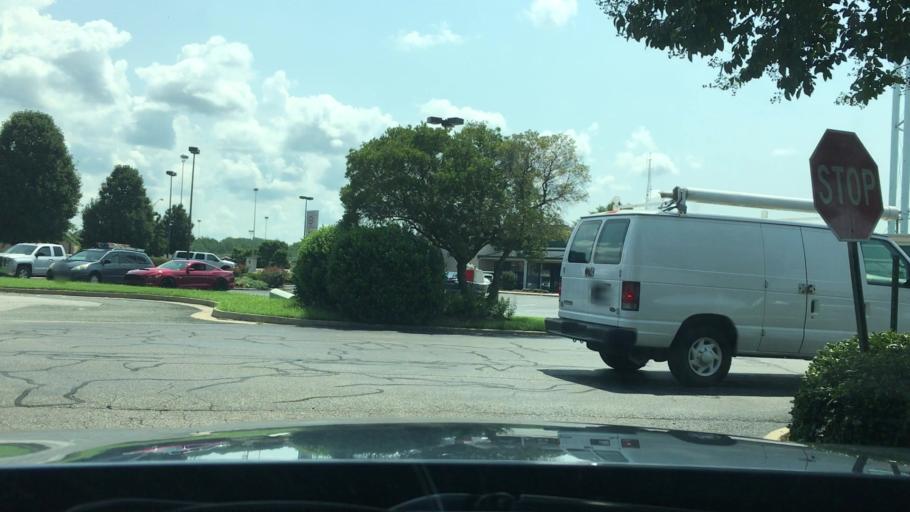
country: US
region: Virginia
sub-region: City of Petersburg
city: Petersburg
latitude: 37.2492
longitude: -77.3901
